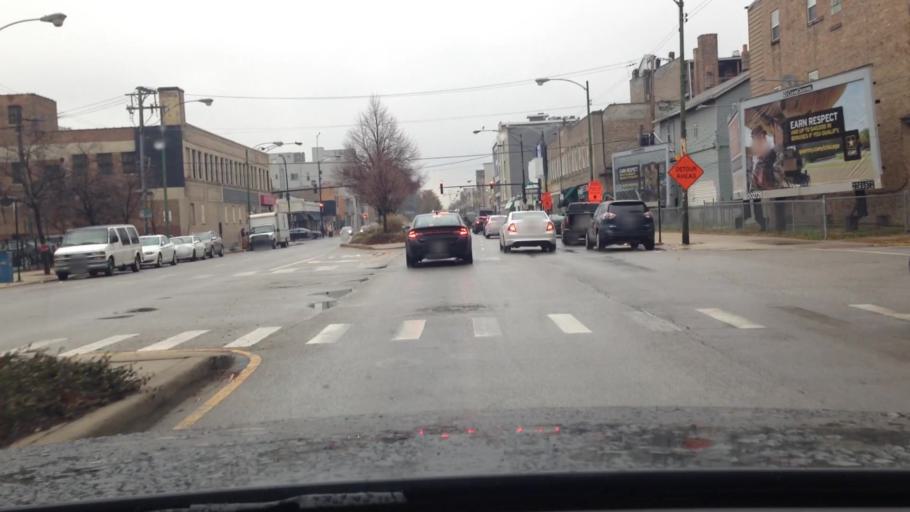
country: US
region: Illinois
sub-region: Cook County
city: Chicago
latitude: 41.8949
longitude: -87.6672
